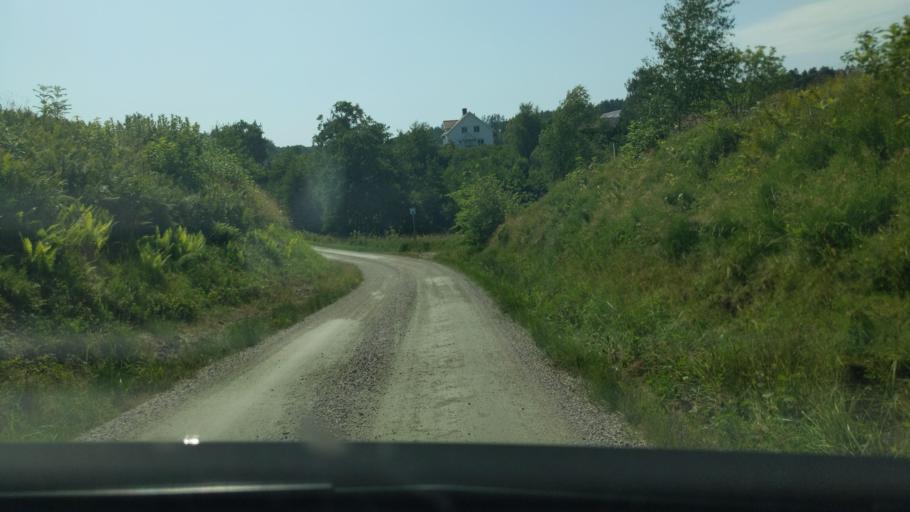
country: SE
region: Vaestra Goetaland
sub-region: Uddevalla Kommun
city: Uddevalla
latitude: 58.3373
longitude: 11.8079
